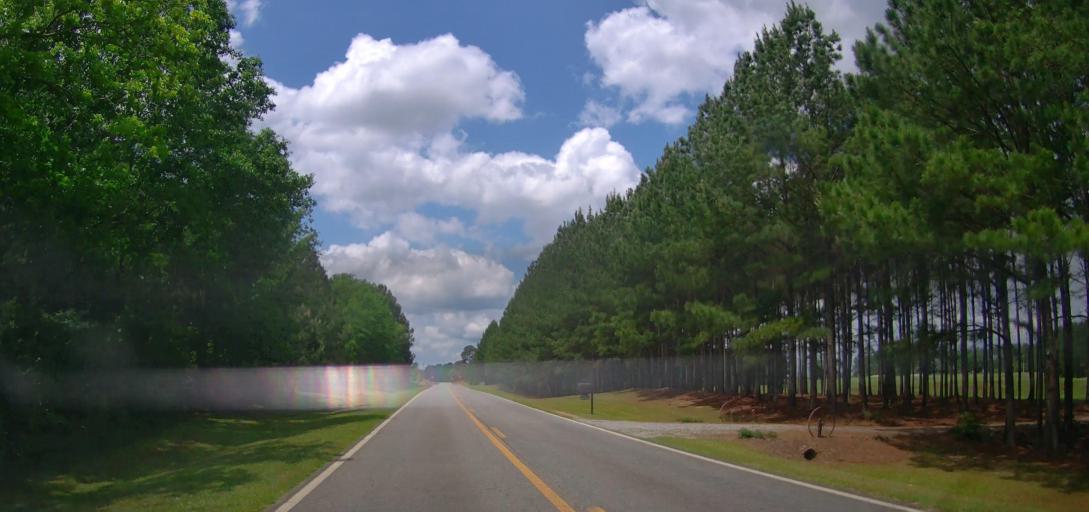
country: US
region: Georgia
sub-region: Laurens County
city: Dublin
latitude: 32.5994
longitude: -83.0039
